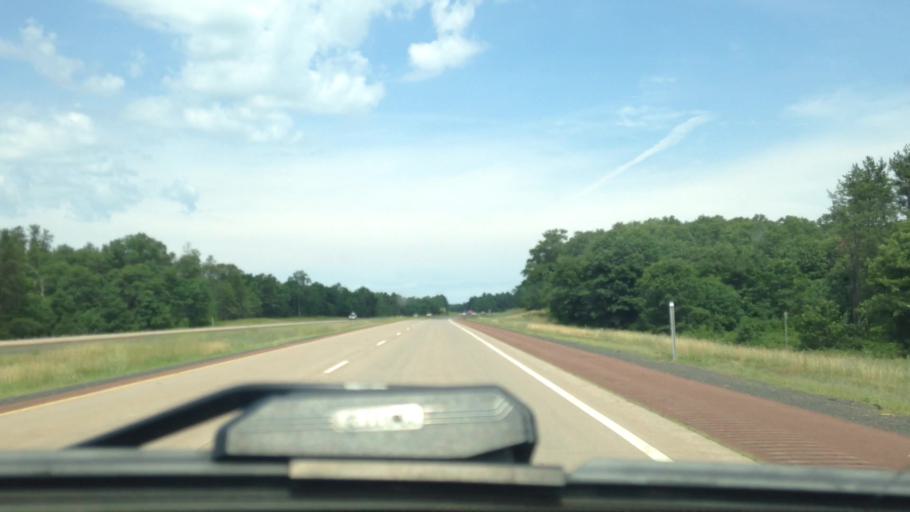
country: US
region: Wisconsin
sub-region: Douglas County
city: Lake Nebagamon
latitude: 46.3340
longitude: -91.8273
